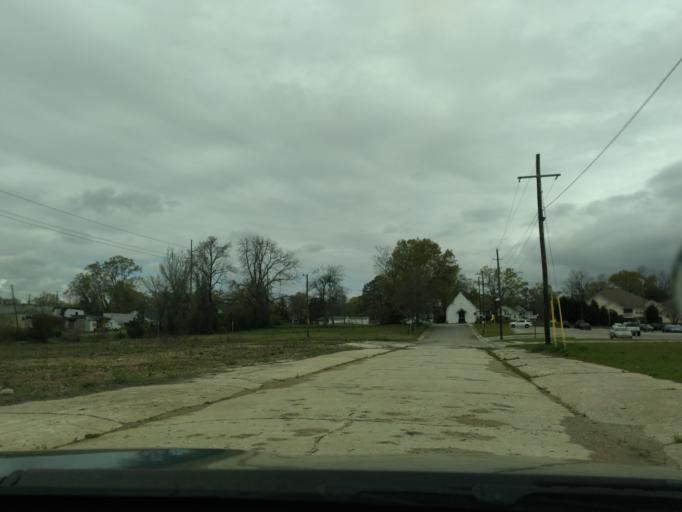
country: US
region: North Carolina
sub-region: Pitt County
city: Greenville
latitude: 35.6098
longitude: -77.3789
